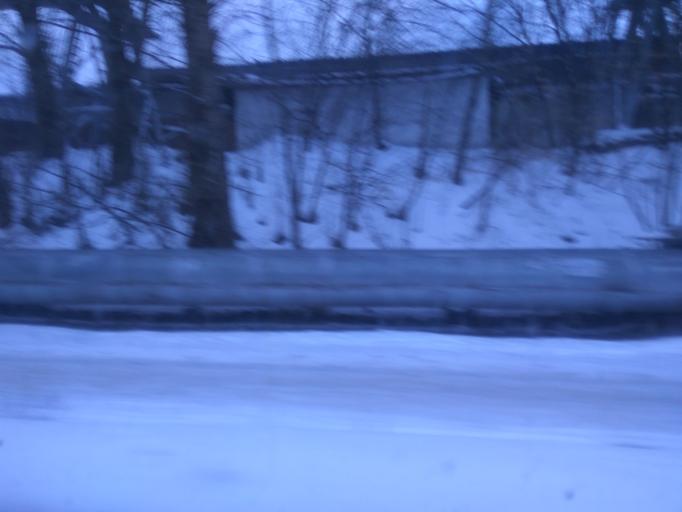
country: RU
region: Moscow
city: Taganskiy
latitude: 55.7289
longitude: 37.6937
